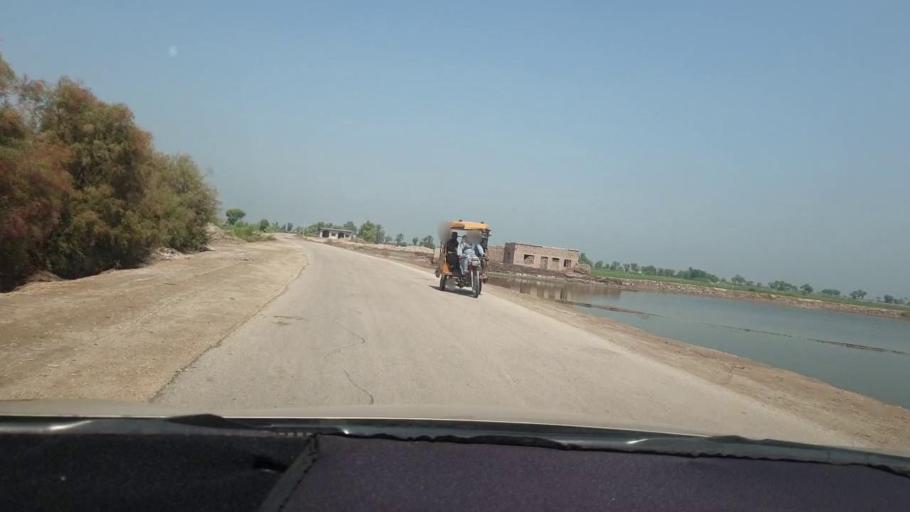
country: PK
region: Sindh
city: Miro Khan
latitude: 27.8162
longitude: 68.0270
